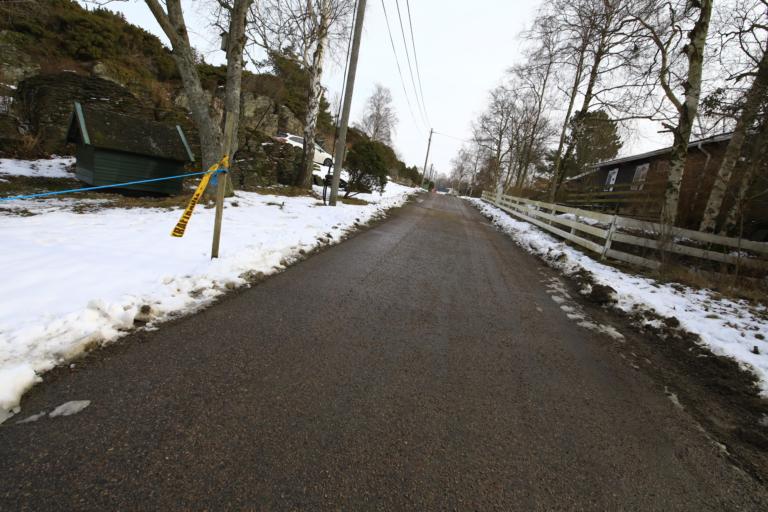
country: SE
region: Halland
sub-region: Kungsbacka Kommun
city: Frillesas
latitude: 57.2163
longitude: 12.1576
